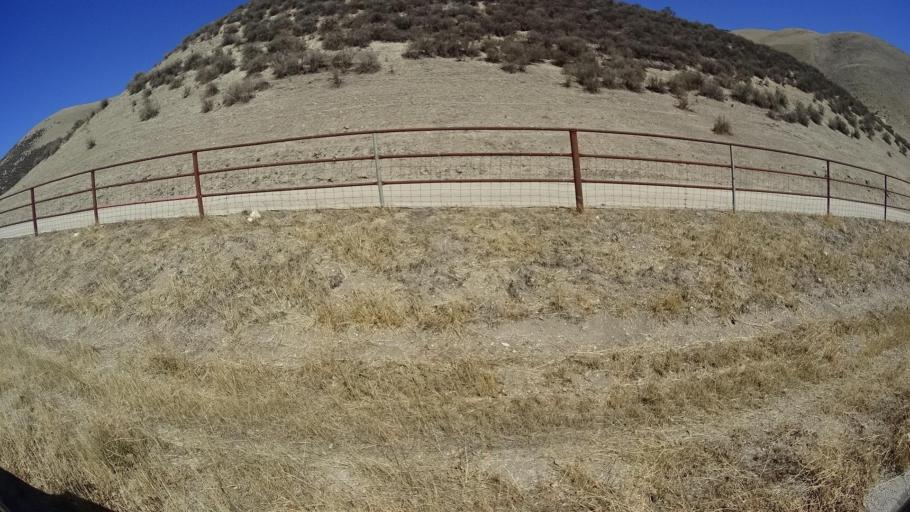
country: US
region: California
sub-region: Monterey County
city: Greenfield
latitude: 36.2718
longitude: -121.3987
